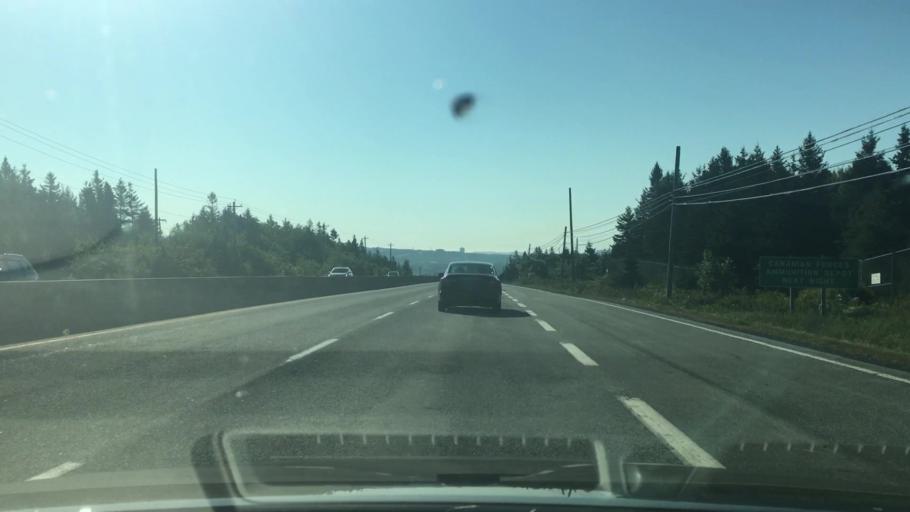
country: CA
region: Nova Scotia
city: Dartmouth
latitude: 44.7180
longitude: -63.6351
